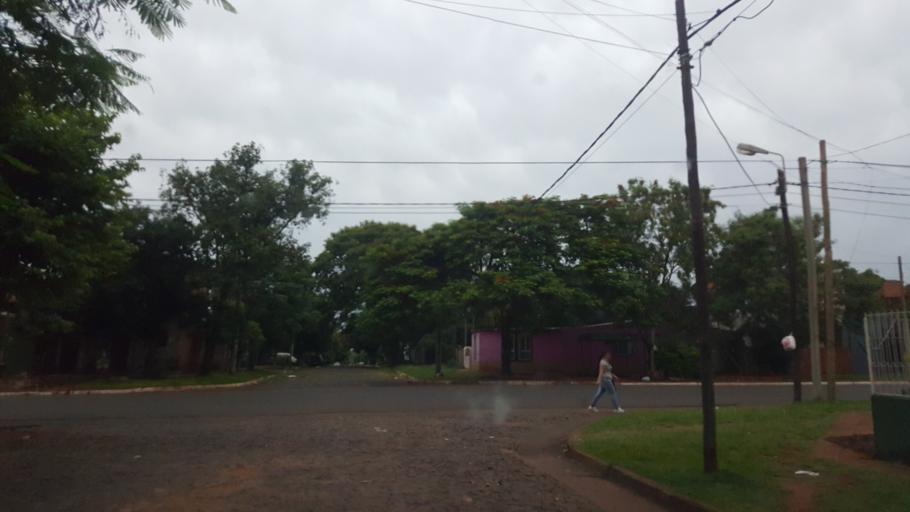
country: AR
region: Misiones
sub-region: Departamento de Capital
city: Posadas
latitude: -27.3778
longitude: -55.9238
